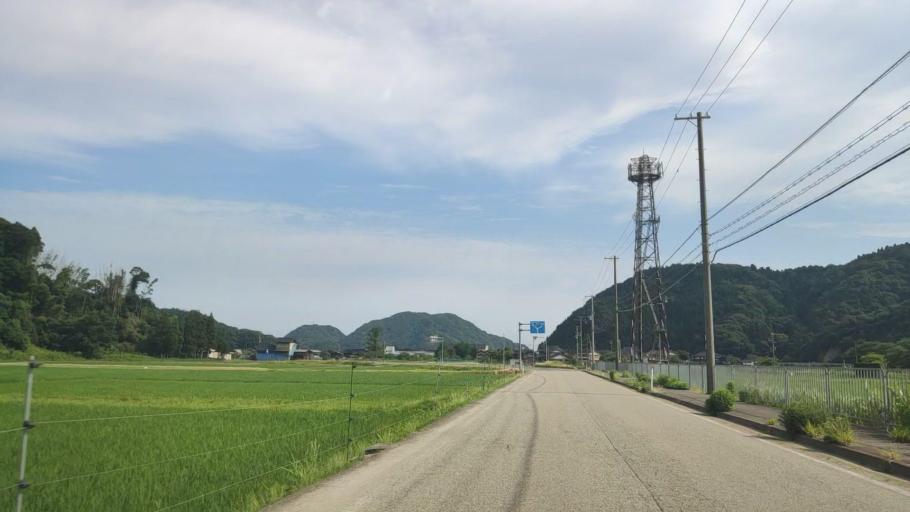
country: JP
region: Hyogo
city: Toyooka
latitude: 35.6310
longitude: 134.8409
